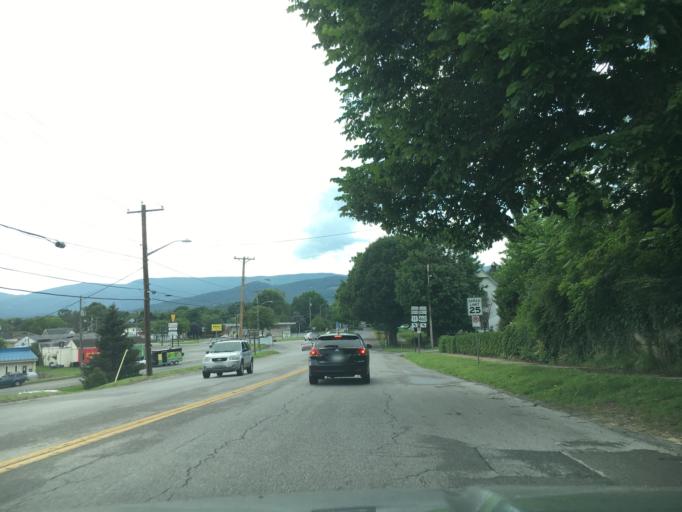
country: US
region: Virginia
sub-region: City of Salem
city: Salem
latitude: 37.2871
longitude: -80.0480
